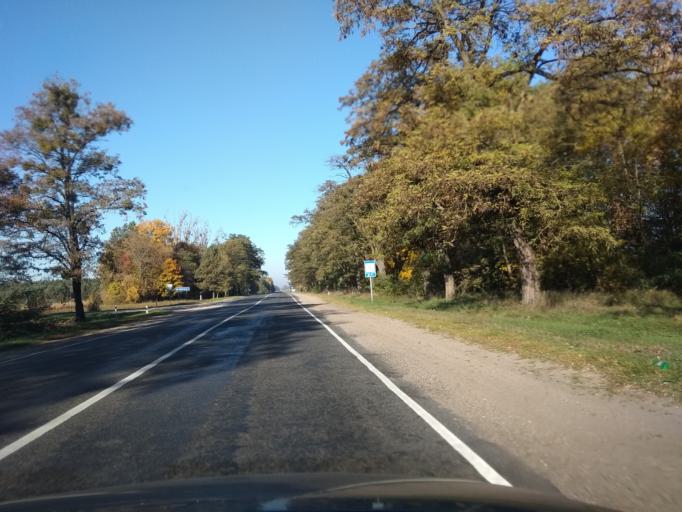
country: BY
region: Brest
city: Malaryta
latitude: 51.9320
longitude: 24.0573
